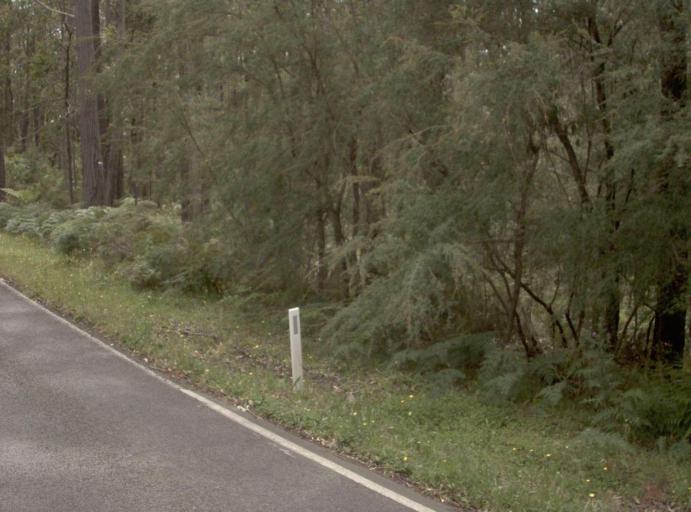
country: AU
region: Victoria
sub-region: Latrobe
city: Traralgon
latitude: -38.0481
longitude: 146.4239
